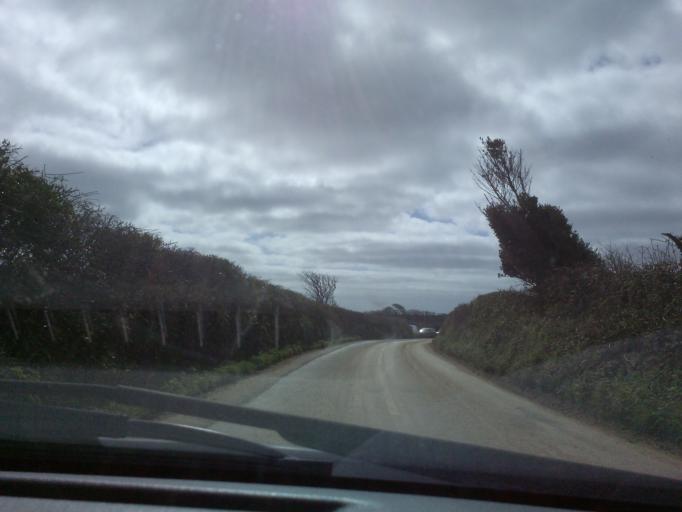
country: GB
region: England
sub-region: Cornwall
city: St. Buryan
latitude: 50.0607
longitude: -5.6058
